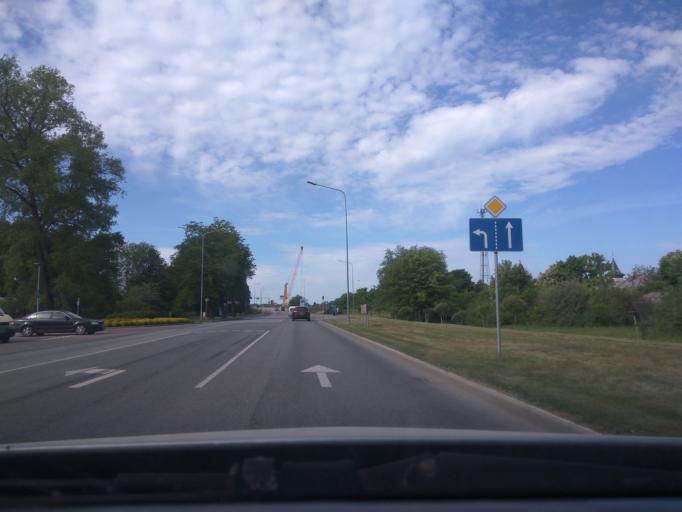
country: LV
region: Ventspils
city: Ventspils
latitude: 57.3913
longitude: 21.5966
